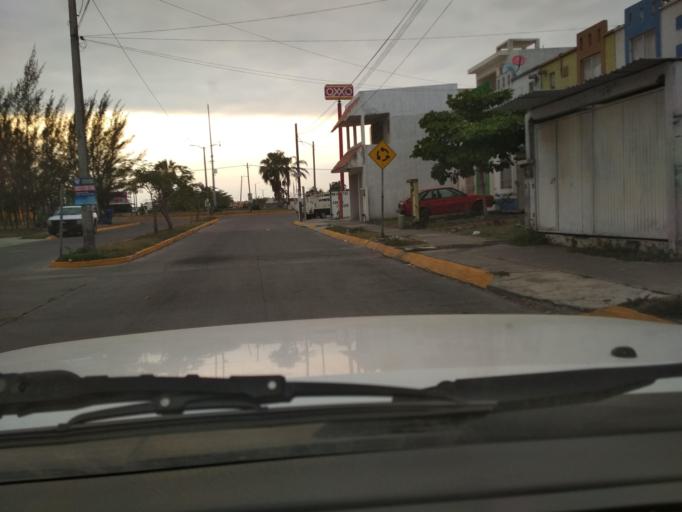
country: MX
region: Veracruz
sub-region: Medellin
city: Fraccionamiento Arboledas San Ramon
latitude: 19.0931
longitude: -96.1542
